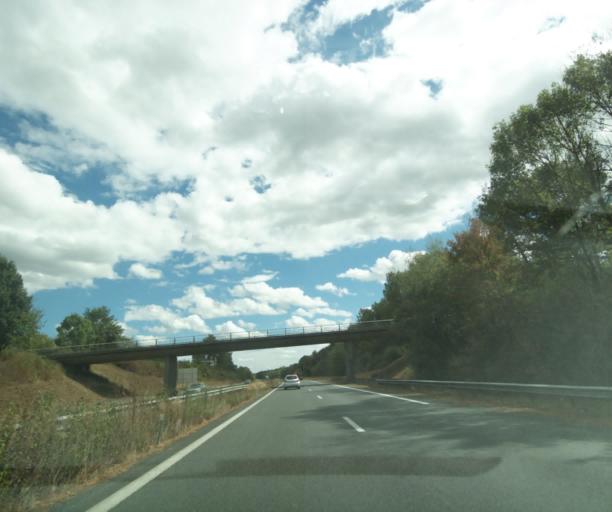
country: FR
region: Aquitaine
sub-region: Departement du Lot-et-Garonne
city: Meilhan-sur-Garonne
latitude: 44.5011
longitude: -0.0313
